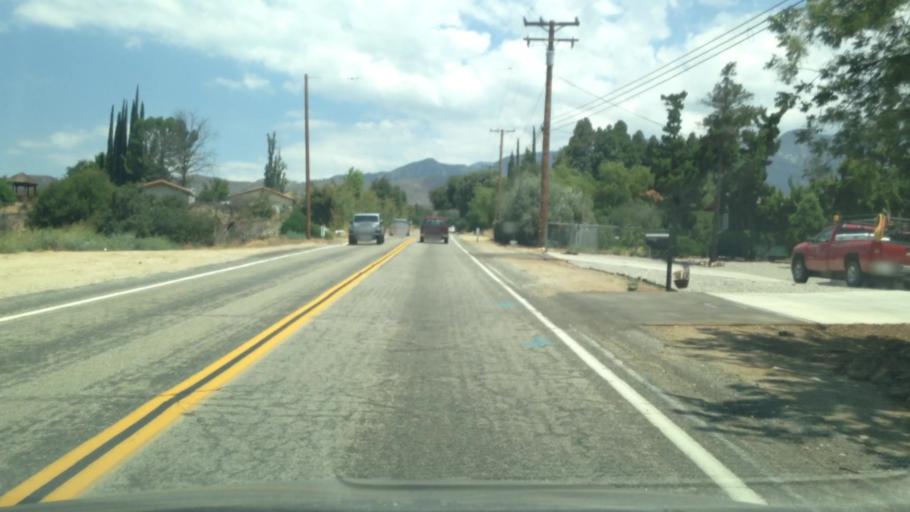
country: US
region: California
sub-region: Riverside County
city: Cherry Valley
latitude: 33.9947
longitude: -116.9632
